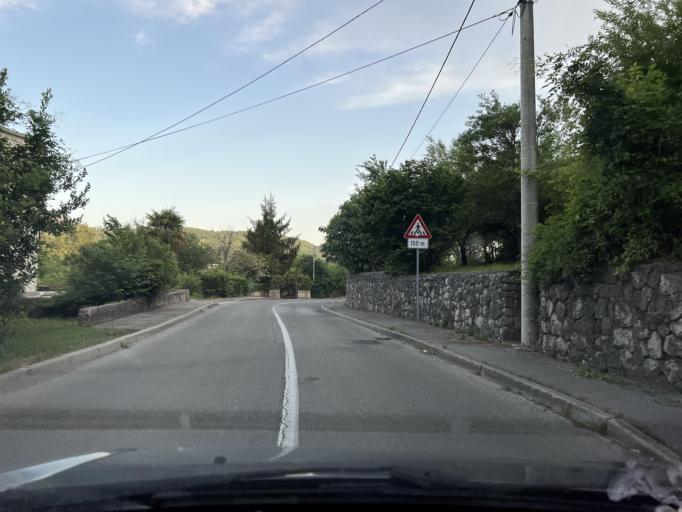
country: HR
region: Primorsko-Goranska
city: Drazice
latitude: 45.3858
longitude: 14.4487
